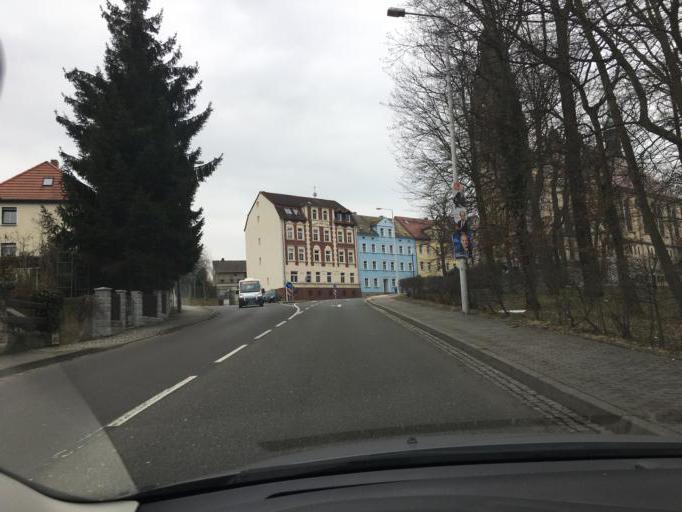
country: DE
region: Thuringia
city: Altenburg
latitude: 50.9906
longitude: 12.4472
